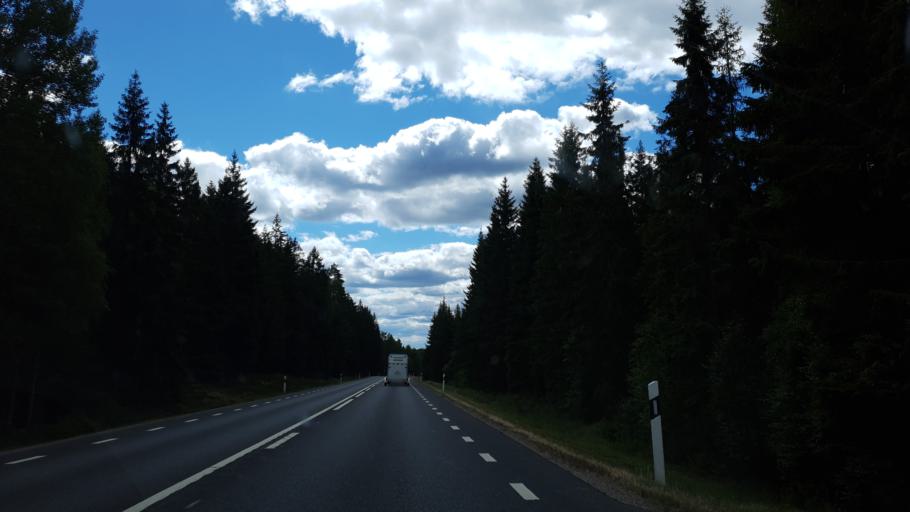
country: SE
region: Joenkoeping
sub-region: Vetlanda Kommun
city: Vetlanda
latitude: 57.2481
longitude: 15.1373
